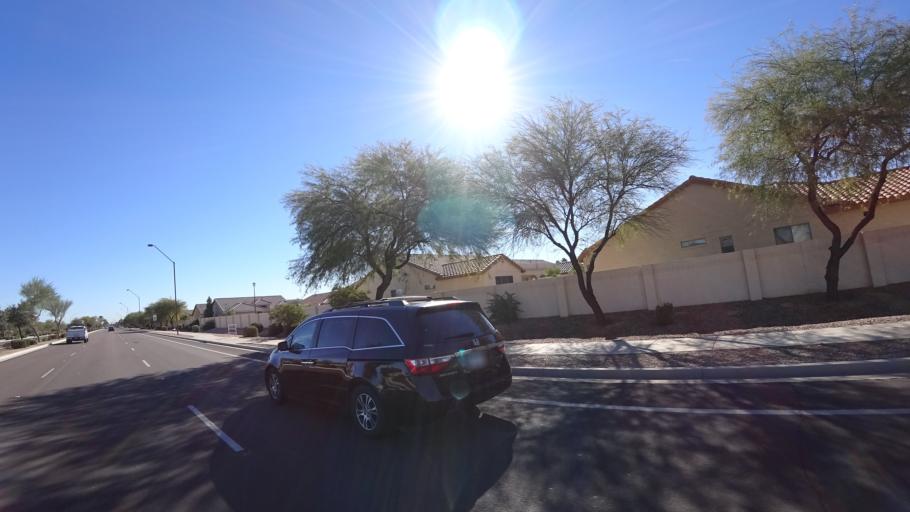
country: US
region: Arizona
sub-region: Maricopa County
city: Litchfield Park
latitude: 33.4936
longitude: -112.4071
